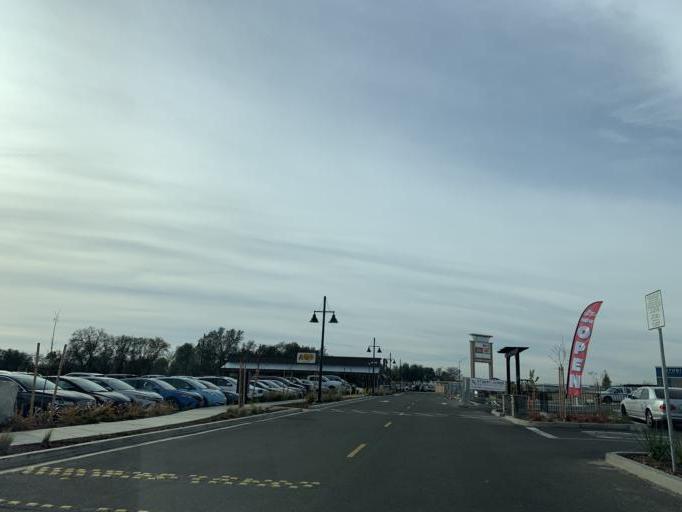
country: US
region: California
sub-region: Placer County
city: Loomis
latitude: 38.7997
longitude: -121.2067
